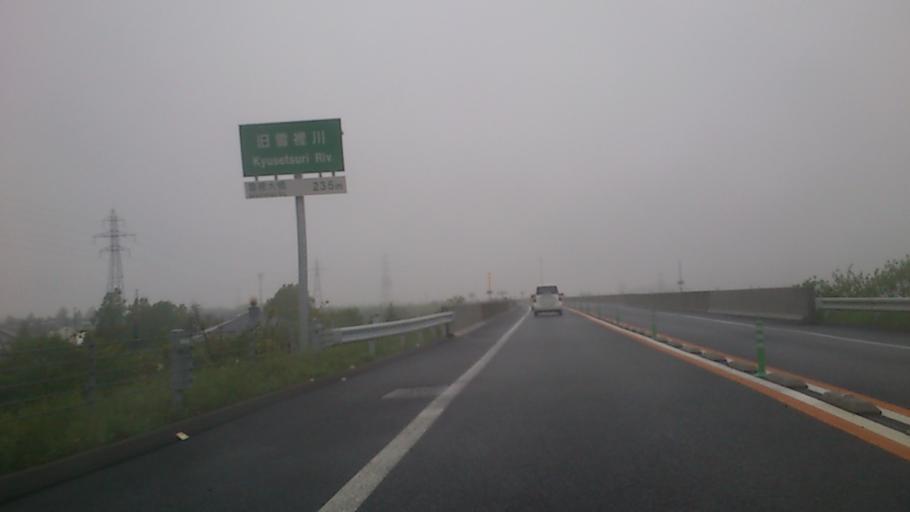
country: JP
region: Hokkaido
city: Kushiro
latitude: 43.0163
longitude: 144.4226
